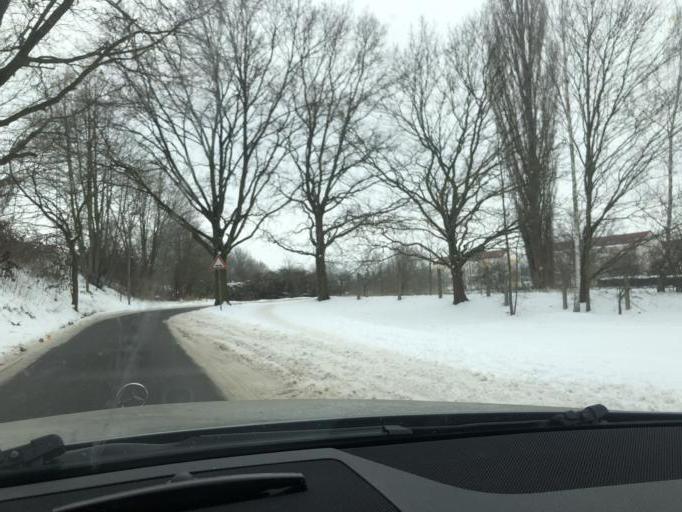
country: DE
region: Brandenburg
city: Guben
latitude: 51.9444
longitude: 14.7126
